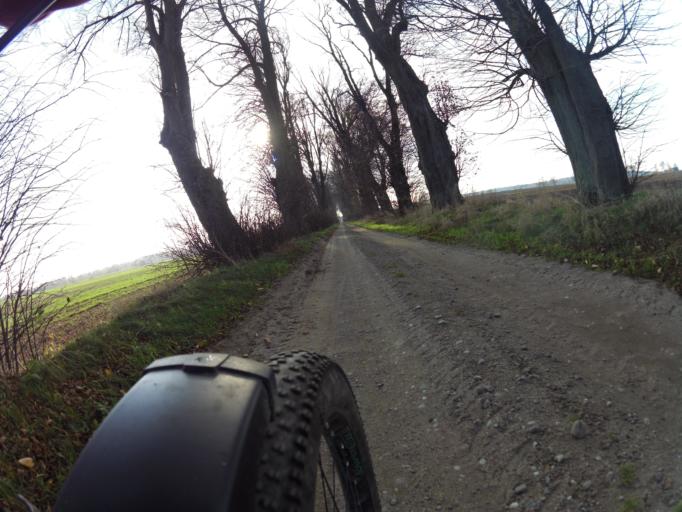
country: PL
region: Pomeranian Voivodeship
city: Strzelno
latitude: 54.7532
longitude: 18.2906
